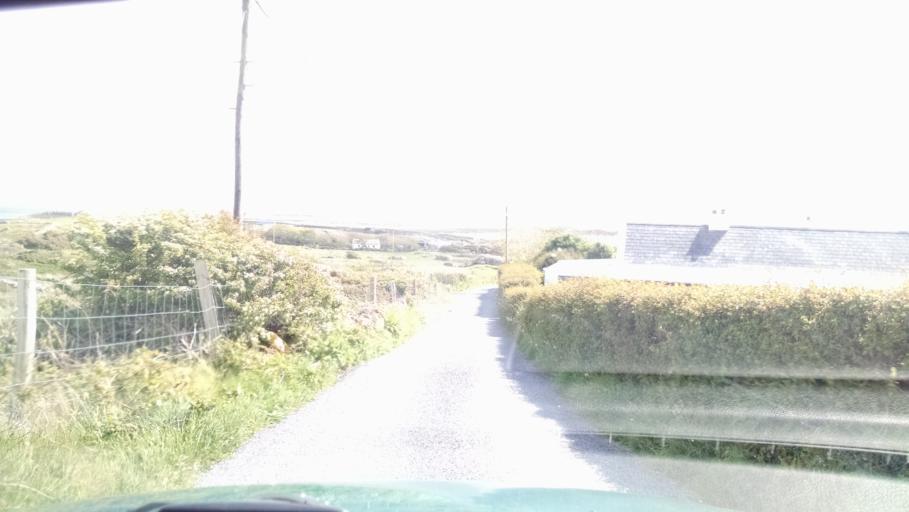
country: IE
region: Connaught
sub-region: County Galway
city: Clifden
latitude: 53.3856
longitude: -9.9625
